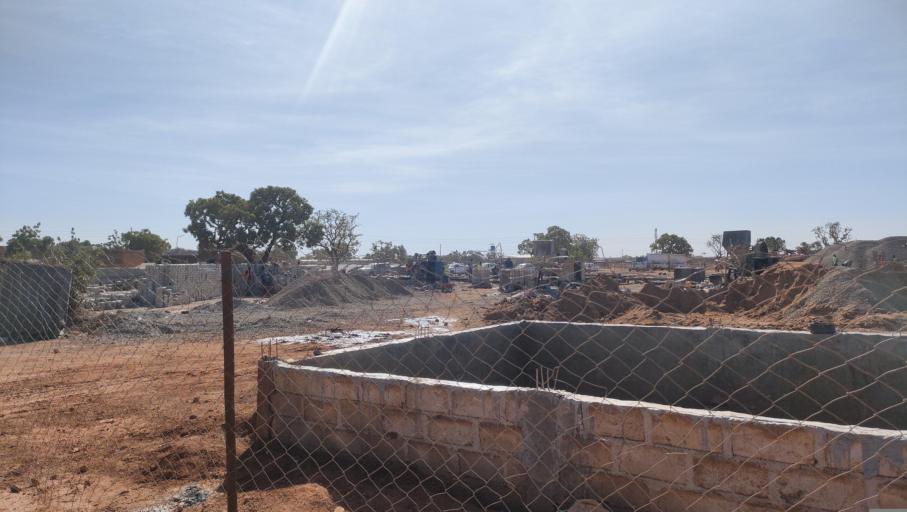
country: BF
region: Est
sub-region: Province du Gourma
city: Fada N'gourma
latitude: 12.0482
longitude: 0.3579
